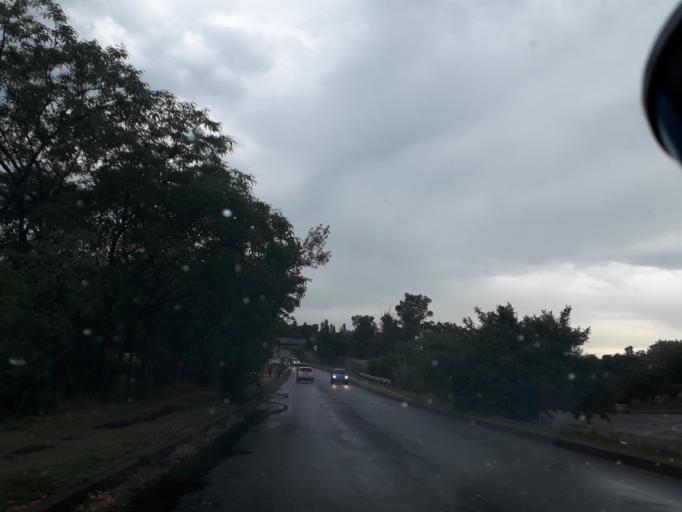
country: ZA
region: Gauteng
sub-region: City of Johannesburg Metropolitan Municipality
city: Johannesburg
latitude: -26.0824
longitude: 27.9883
